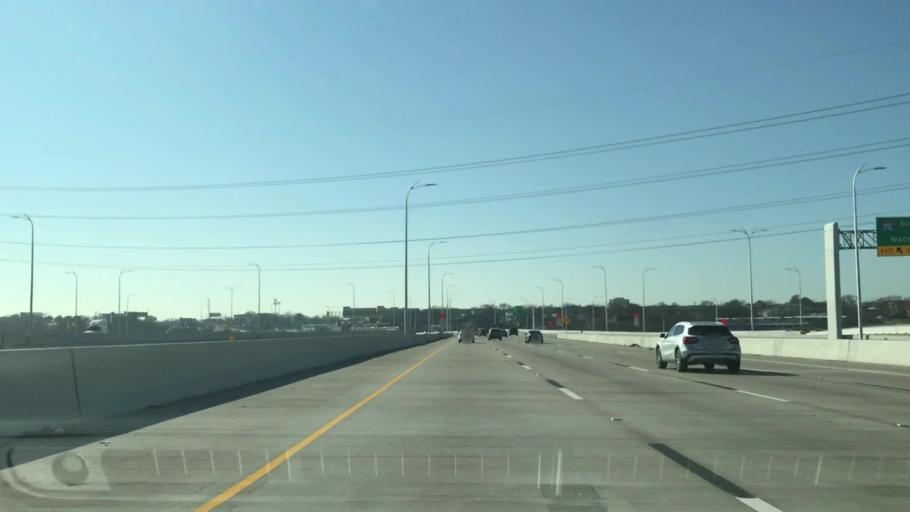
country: US
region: Texas
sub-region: Dallas County
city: Dallas
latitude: 32.7618
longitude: -96.8082
